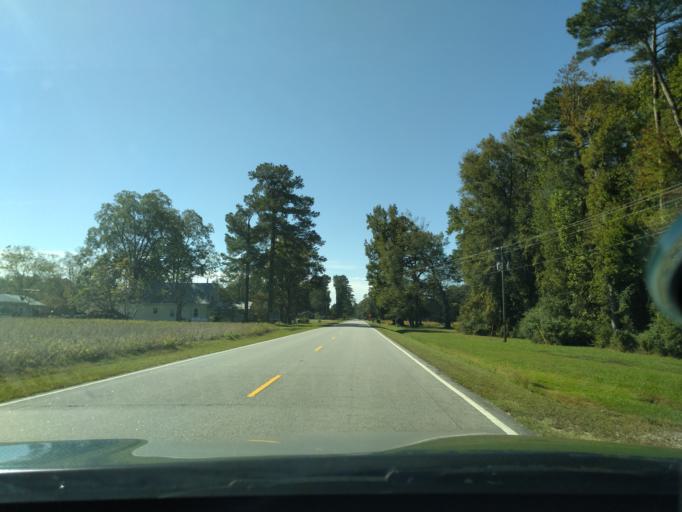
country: US
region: North Carolina
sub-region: Washington County
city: Plymouth
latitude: 35.7098
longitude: -76.7602
